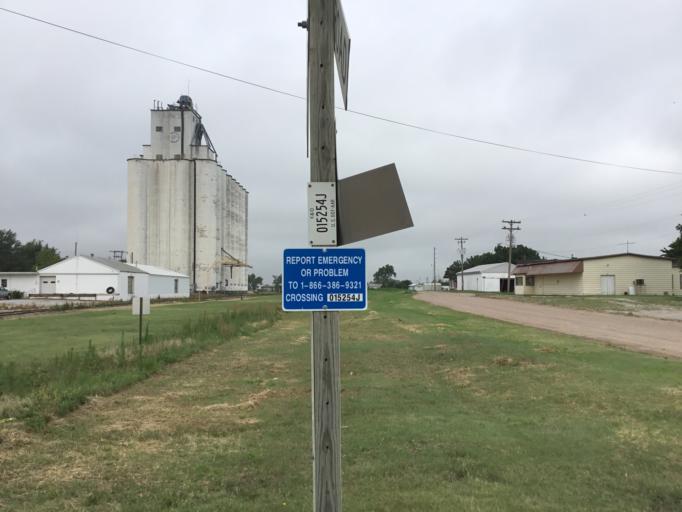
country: US
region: Kansas
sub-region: Pratt County
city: Pratt
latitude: 37.6442
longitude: -98.4318
